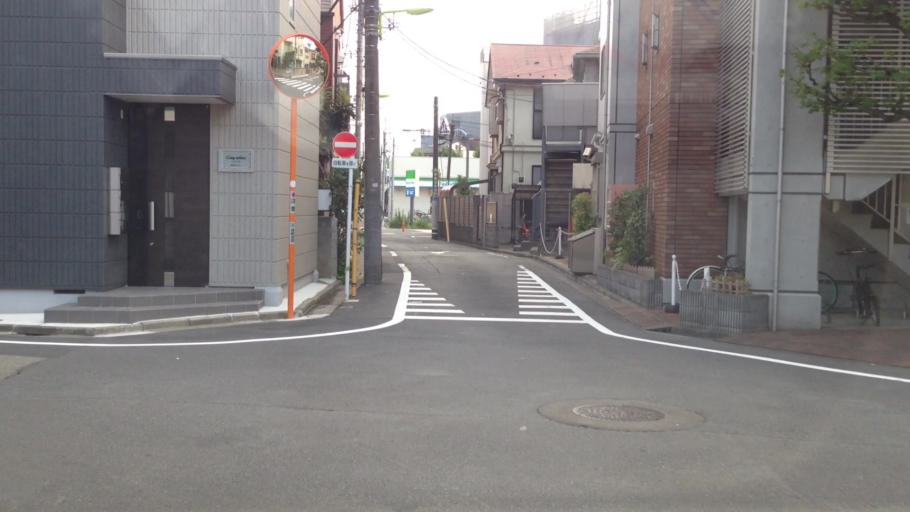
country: JP
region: Tokyo
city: Tokyo
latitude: 35.6300
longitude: 139.6812
